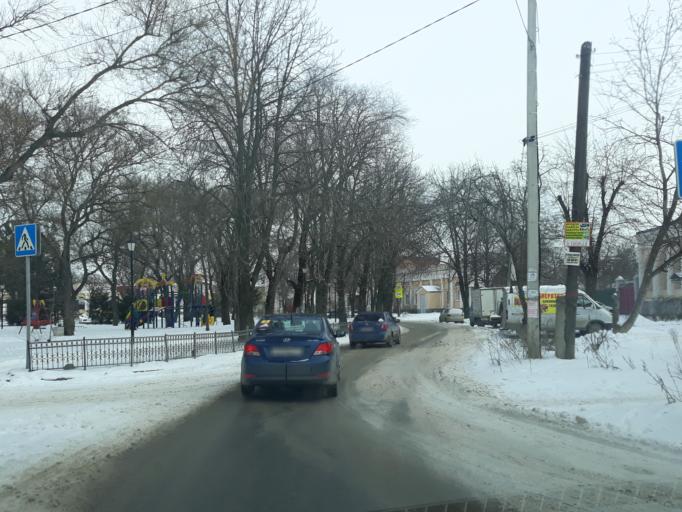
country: RU
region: Rostov
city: Taganrog
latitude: 47.2101
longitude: 38.9206
